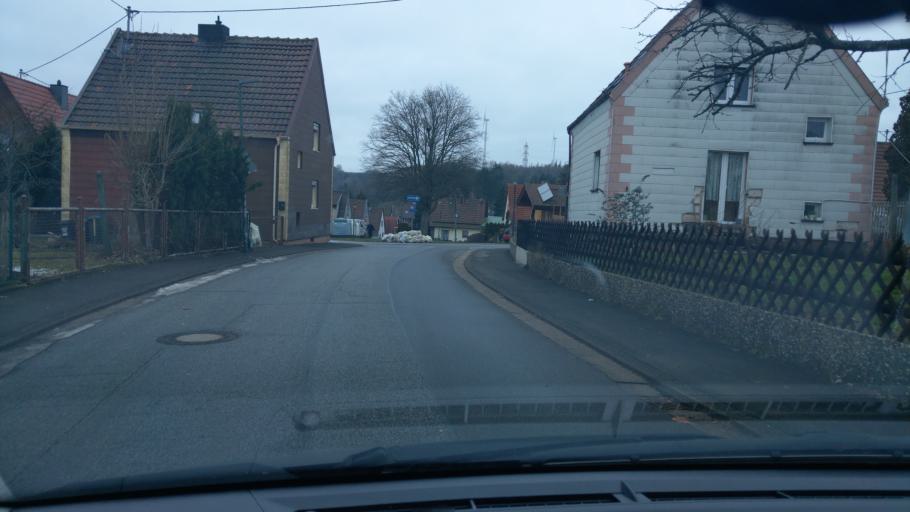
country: DE
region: Saarland
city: Ottweiler
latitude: 49.3727
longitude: 7.1691
